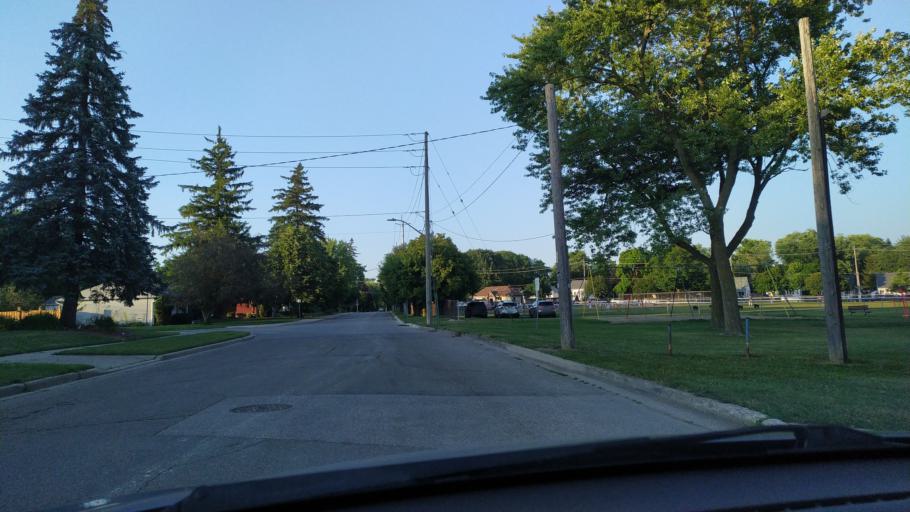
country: CA
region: Ontario
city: Stratford
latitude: 43.3578
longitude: -80.9883
